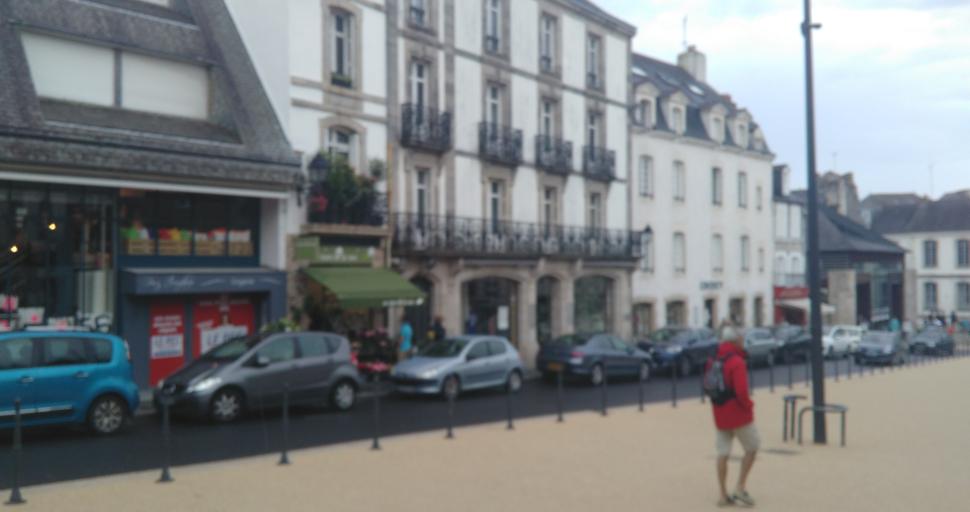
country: FR
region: Brittany
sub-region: Departement du Morbihan
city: Vannes
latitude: 47.6565
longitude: -2.7573
